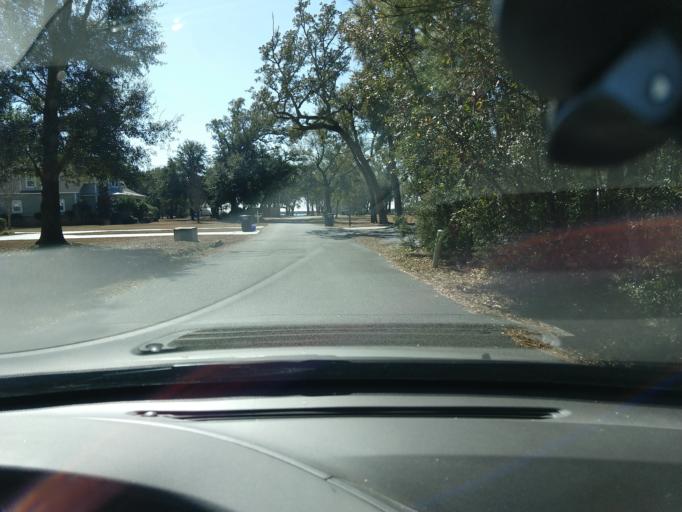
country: US
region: Mississippi
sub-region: Jackson County
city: Gulf Park Estates
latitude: 30.3886
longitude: -88.7888
